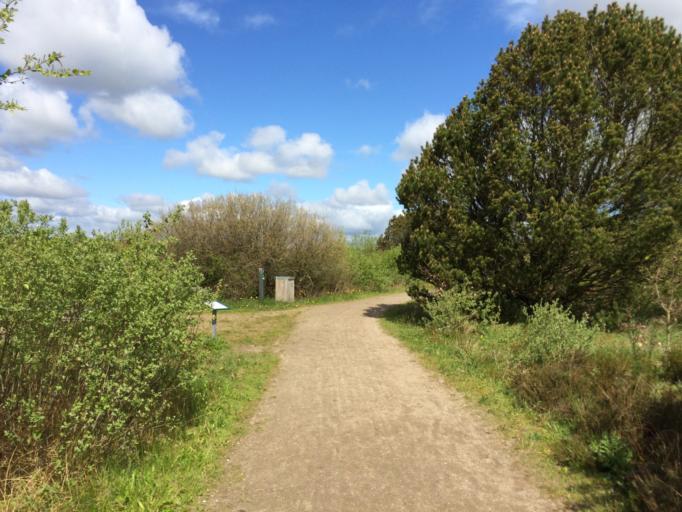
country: DK
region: Central Jutland
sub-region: Holstebro Kommune
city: Holstebro
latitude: 56.2263
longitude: 8.6187
